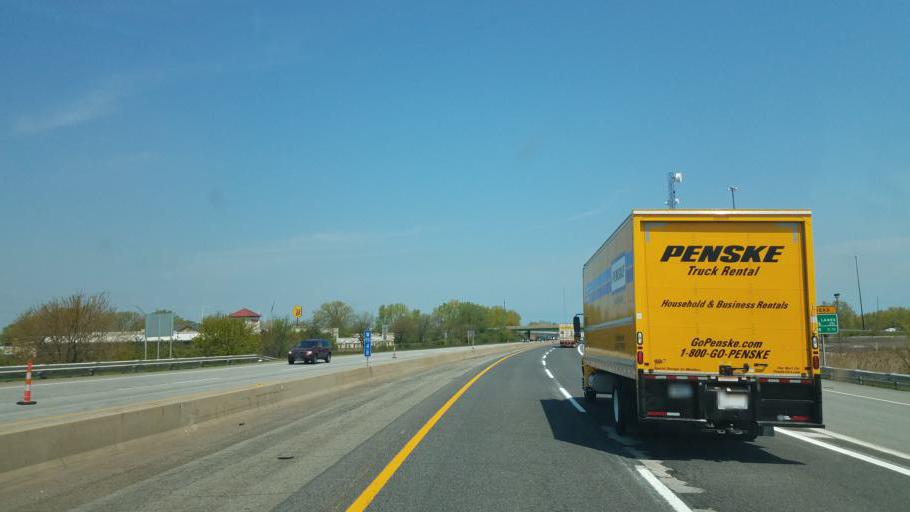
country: US
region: Illinois
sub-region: Cook County
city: Calumet City
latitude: 41.6361
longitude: -87.5060
